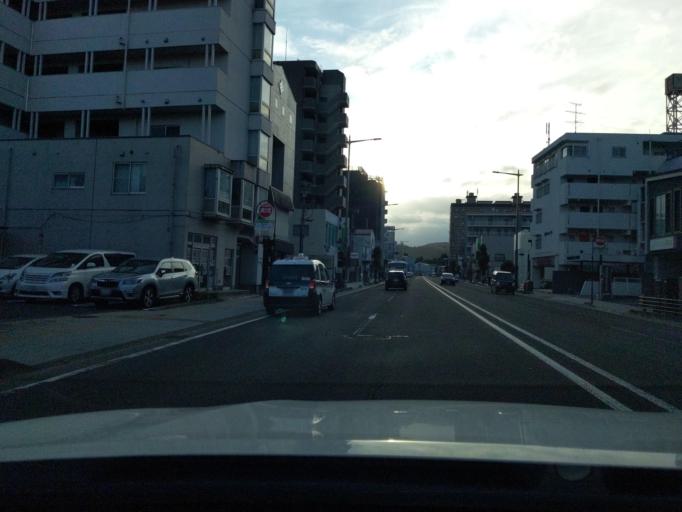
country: JP
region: Miyagi
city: Sendai
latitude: 38.2698
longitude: 140.8480
